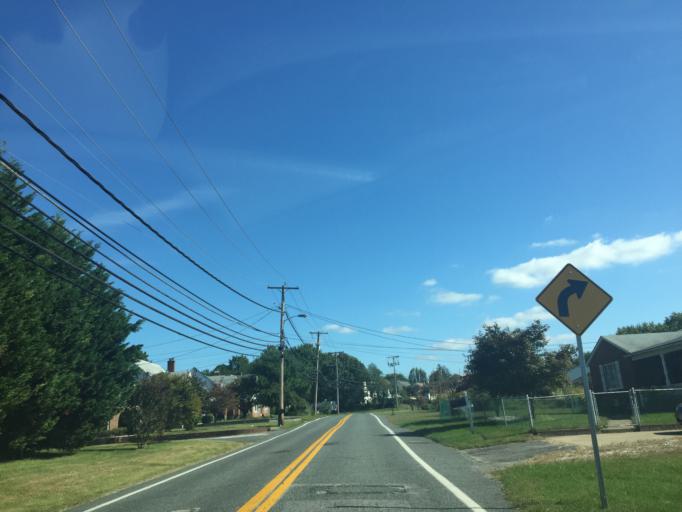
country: US
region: Maryland
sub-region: Baltimore County
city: Overlea
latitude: 39.3728
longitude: -76.5016
